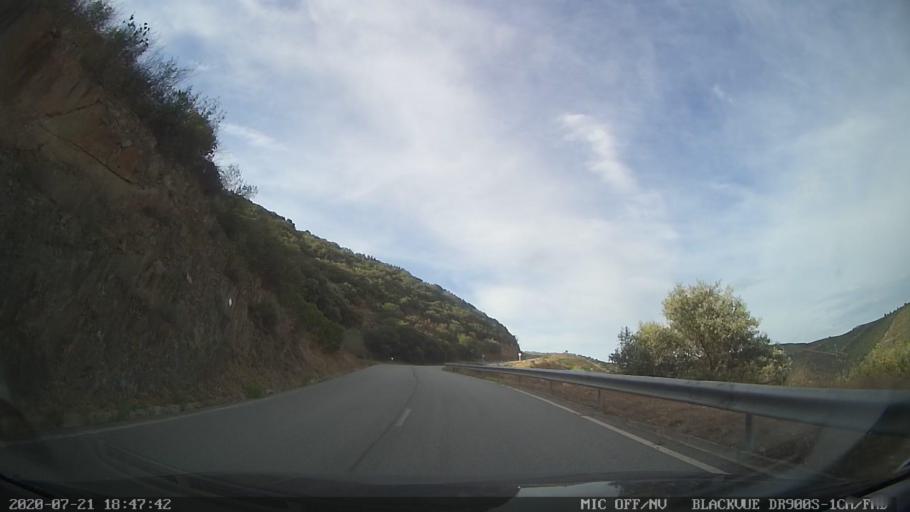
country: PT
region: Viseu
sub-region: Sao Joao da Pesqueira
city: Sao Joao da Pesqueira
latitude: 41.1233
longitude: -7.4372
